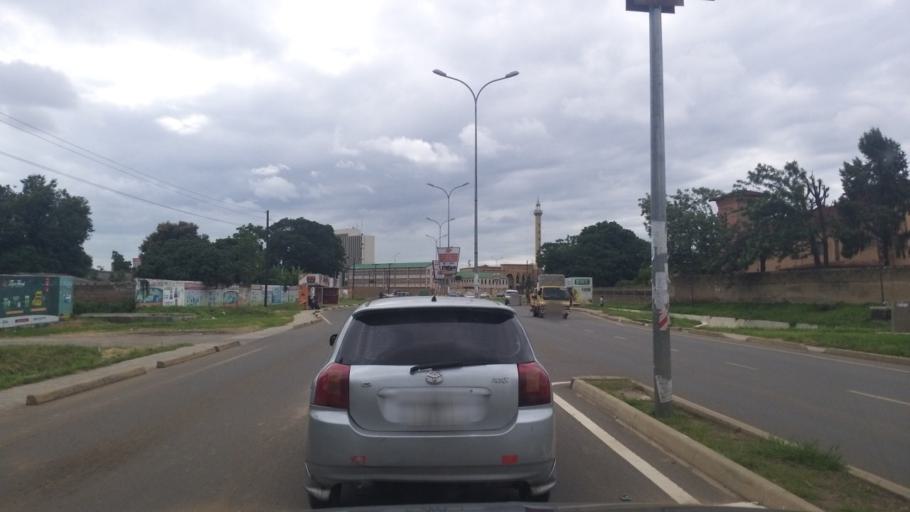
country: ZM
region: Lusaka
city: Lusaka
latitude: -15.4253
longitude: 28.2965
